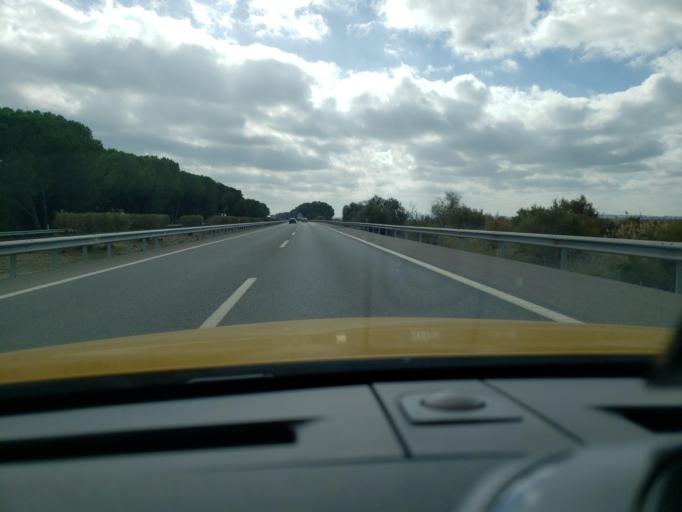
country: ES
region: Andalusia
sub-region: Provincia de Sevilla
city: Las Cabezas de San Juan
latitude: 37.0708
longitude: -5.9361
